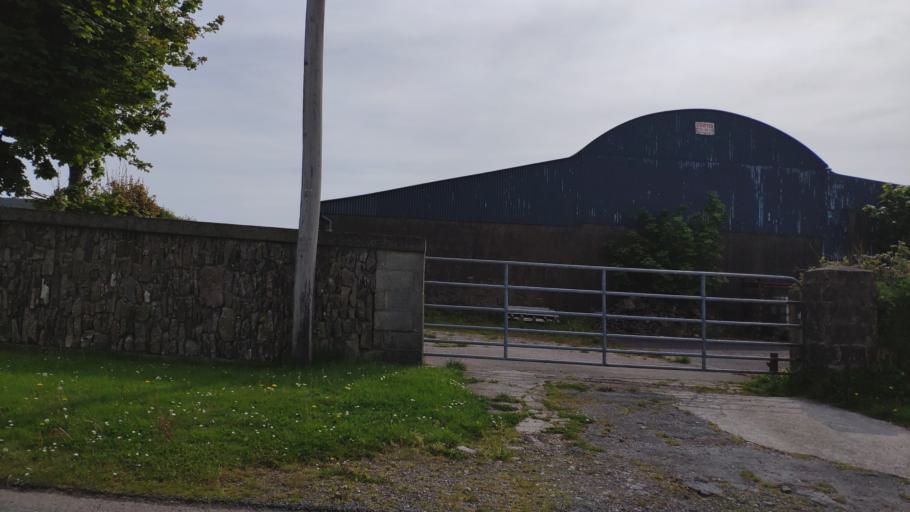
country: IE
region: Munster
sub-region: County Cork
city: Blarney
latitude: 51.9704
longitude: -8.5132
